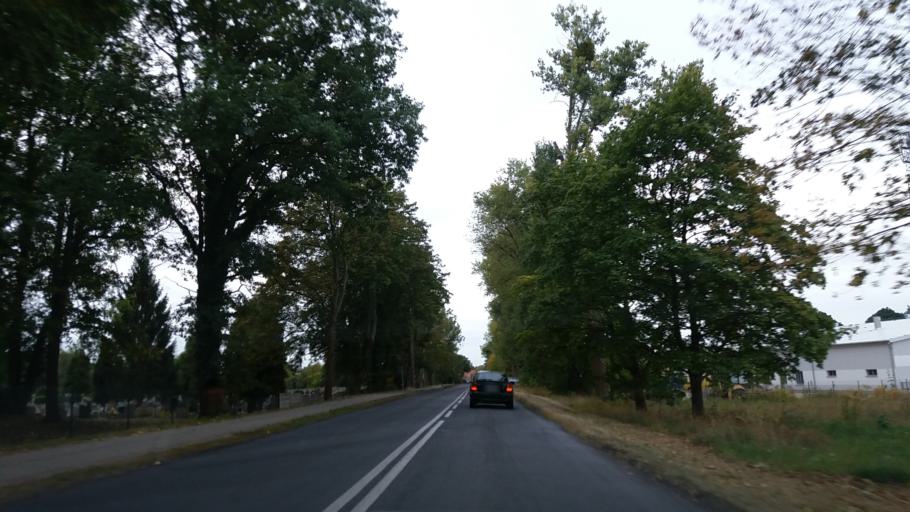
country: PL
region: Lubusz
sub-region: Powiat gorzowski
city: Klodawa
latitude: 52.7944
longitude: 15.2166
